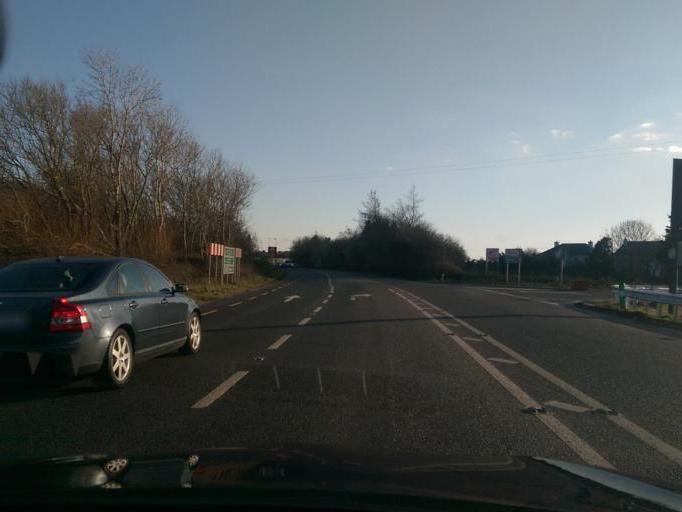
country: IE
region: Connaught
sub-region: County Galway
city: Oranmore
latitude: 53.2639
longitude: -8.9227
